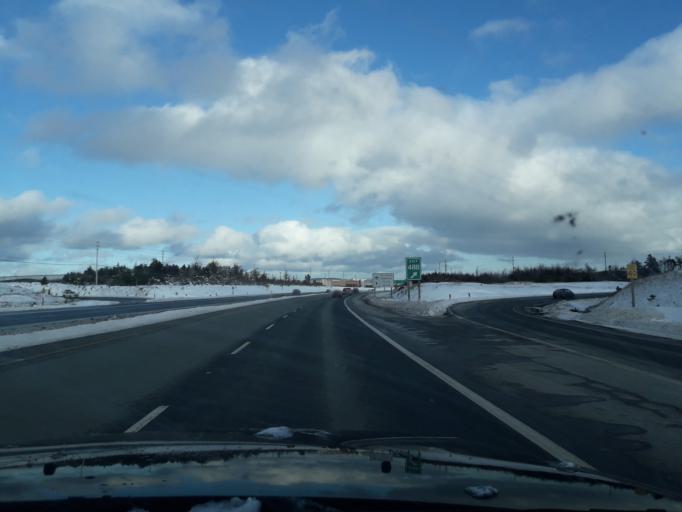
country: CA
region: Newfoundland and Labrador
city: St. John's
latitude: 47.6105
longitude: -52.7216
